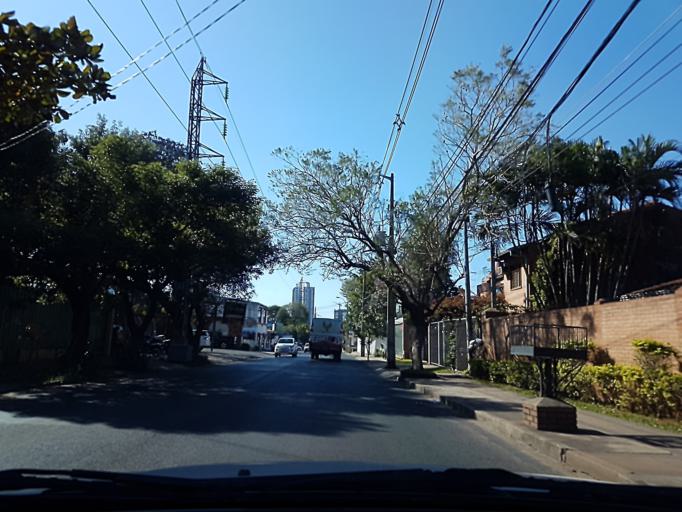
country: PY
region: Central
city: Fernando de la Mora
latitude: -25.2946
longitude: -57.5613
